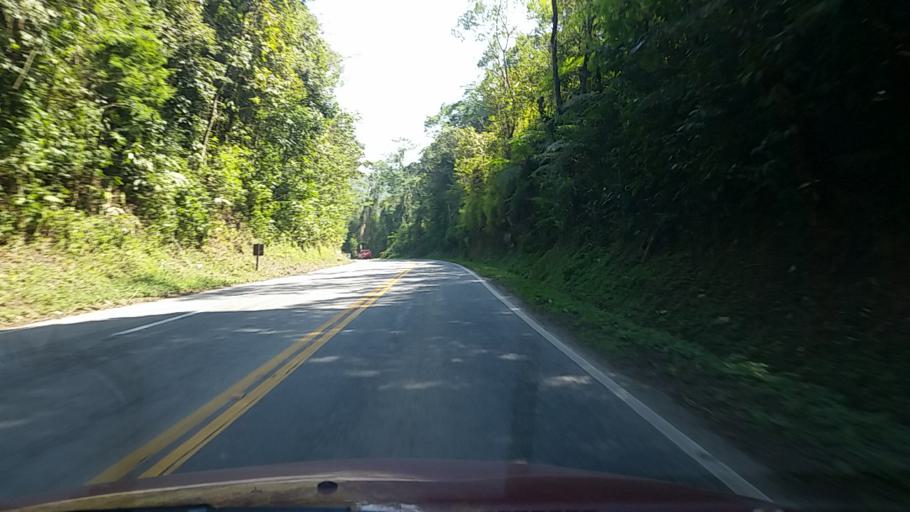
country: BR
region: Sao Paulo
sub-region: Miracatu
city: Miracatu
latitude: -24.3579
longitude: -47.4948
